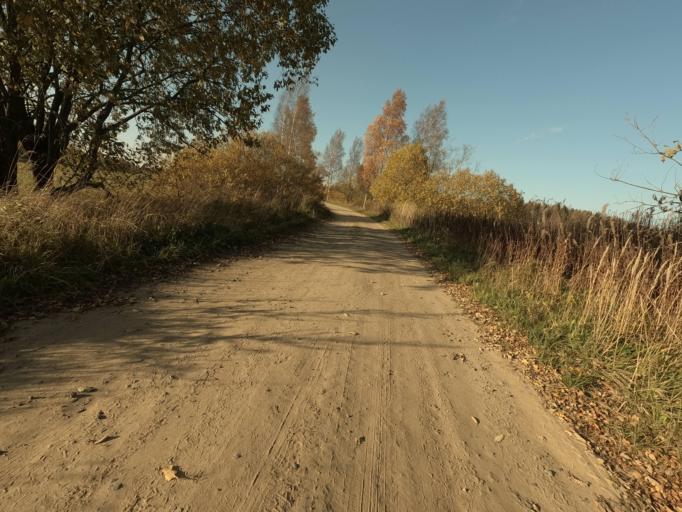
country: RU
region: Leningrad
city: Luppolovo
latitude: 60.1417
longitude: 30.2516
